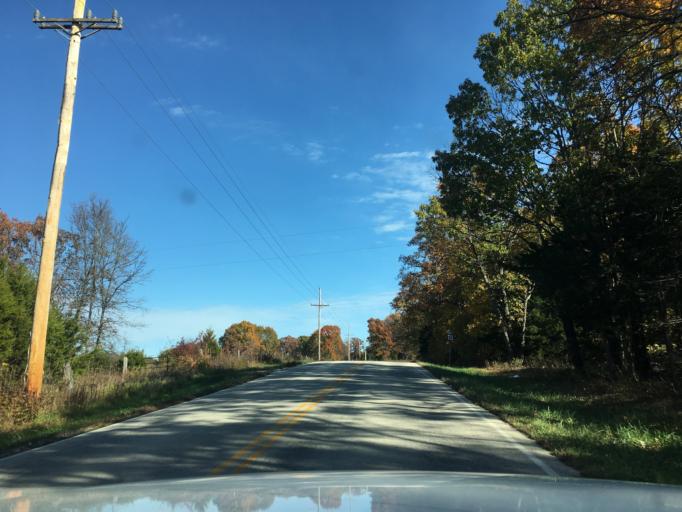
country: US
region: Missouri
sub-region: Maries County
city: Belle
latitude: 38.3369
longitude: -91.7666
